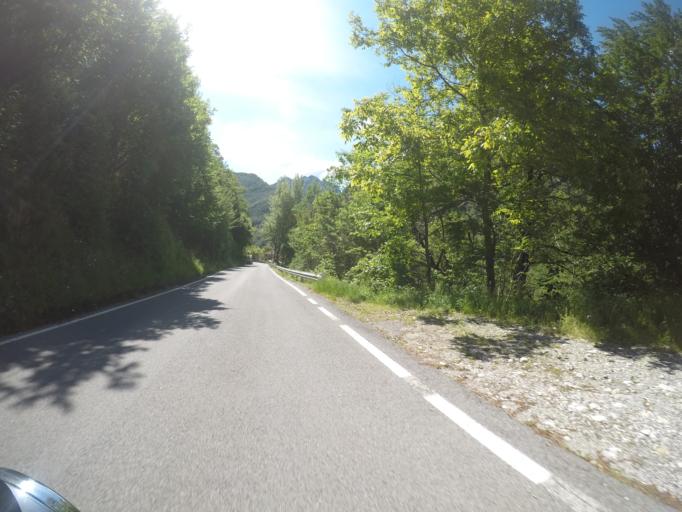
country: IT
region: Tuscany
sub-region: Provincia di Lucca
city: Fontana delle Monache
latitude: 44.0613
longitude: 10.2537
